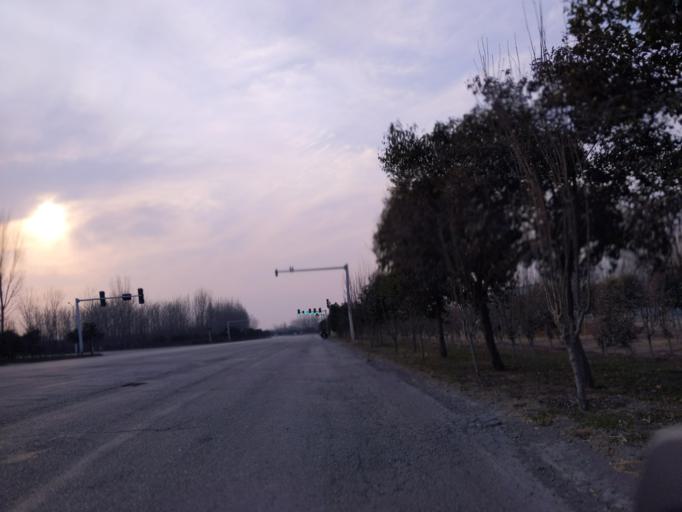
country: CN
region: Henan Sheng
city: Puyang
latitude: 35.8201
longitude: 114.9821
